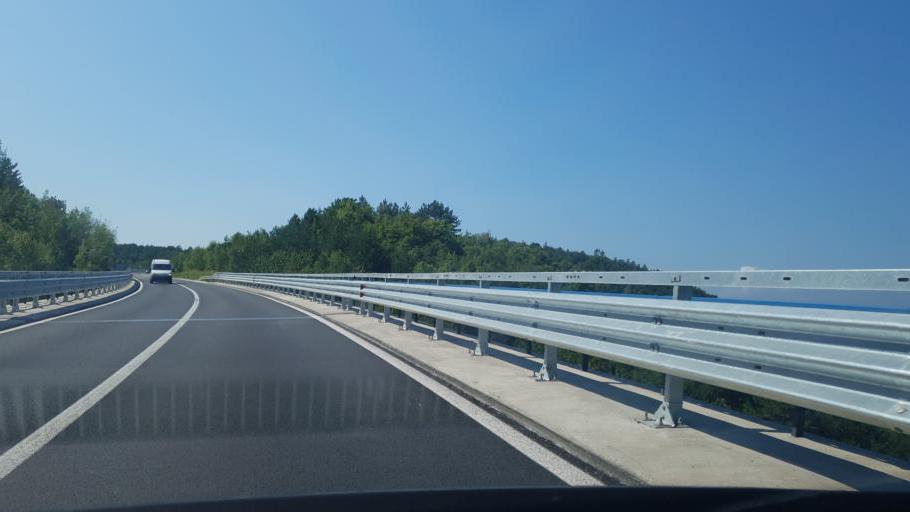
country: HR
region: Istarska
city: Buzet
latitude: 45.3413
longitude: 14.0784
